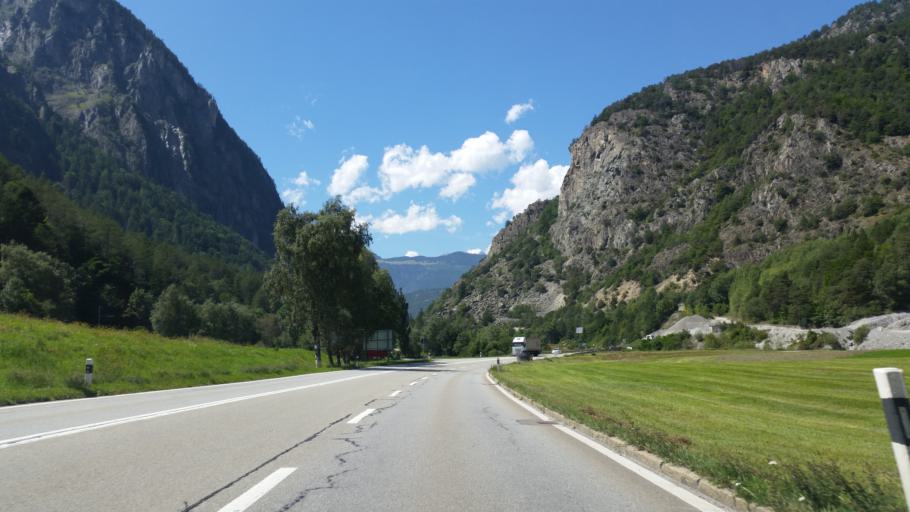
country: CH
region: Valais
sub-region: Martigny District
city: Charrat-les-Chenes
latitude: 46.0781
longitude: 7.1348
